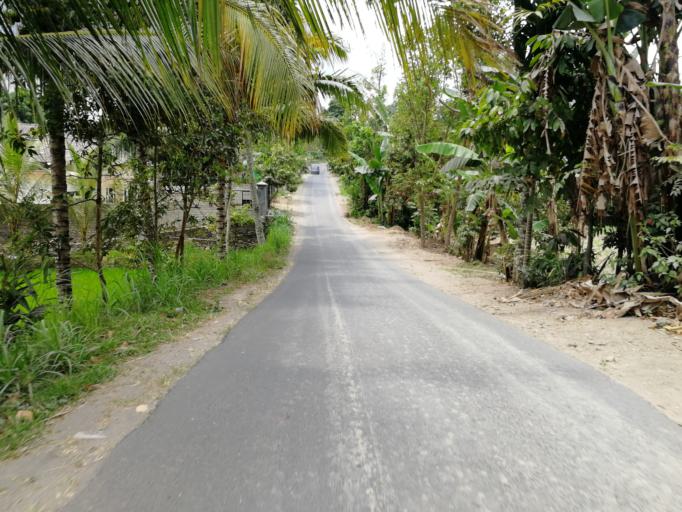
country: ID
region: West Nusa Tenggara
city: Pediti
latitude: -8.5665
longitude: 116.3308
